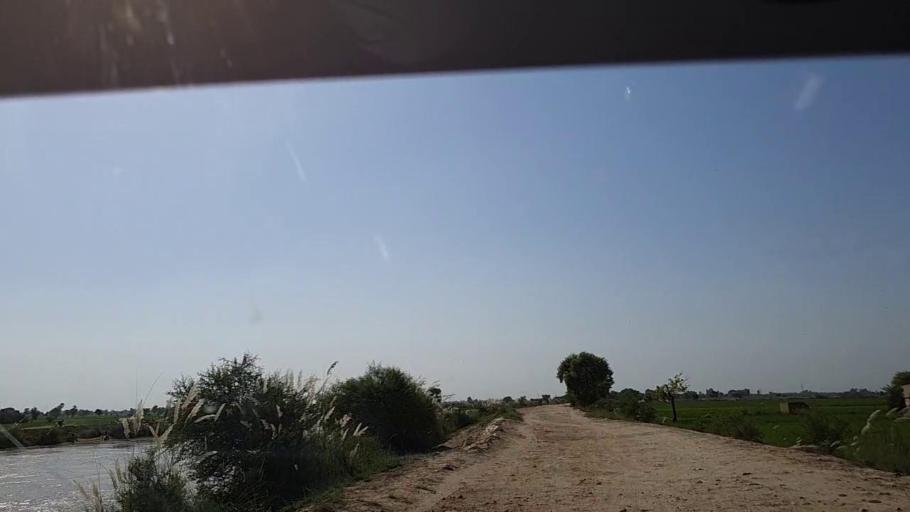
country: PK
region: Sindh
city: Ghauspur
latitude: 28.1761
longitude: 69.0964
